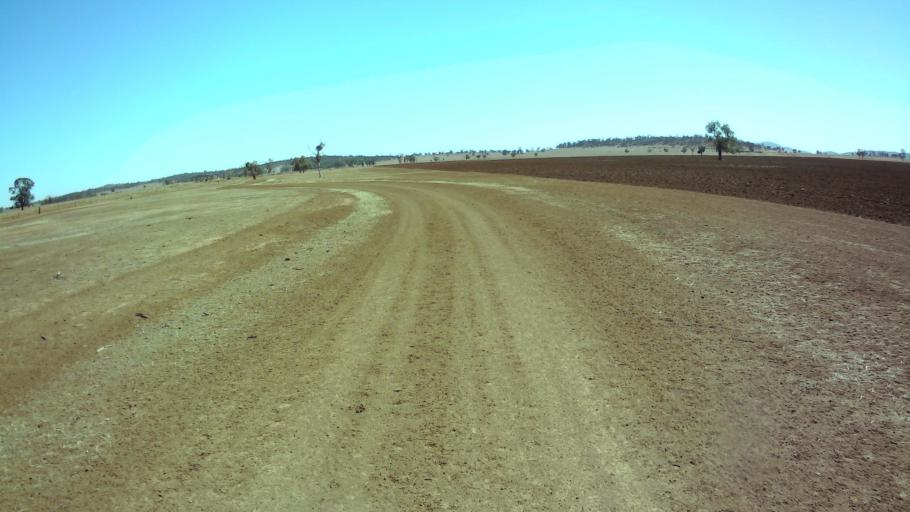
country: AU
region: New South Wales
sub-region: Forbes
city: Forbes
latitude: -33.7101
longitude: 147.6677
